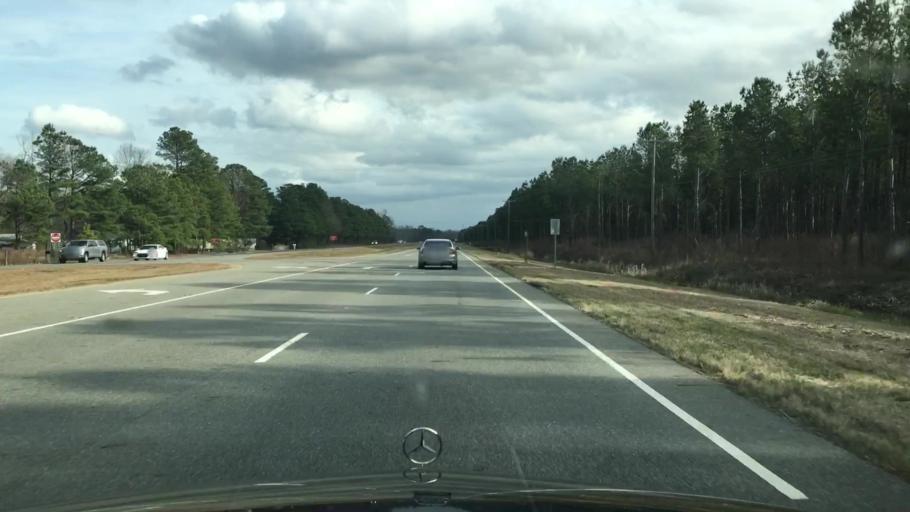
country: US
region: North Carolina
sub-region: Duplin County
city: Kenansville
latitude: 34.9510
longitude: -77.8929
